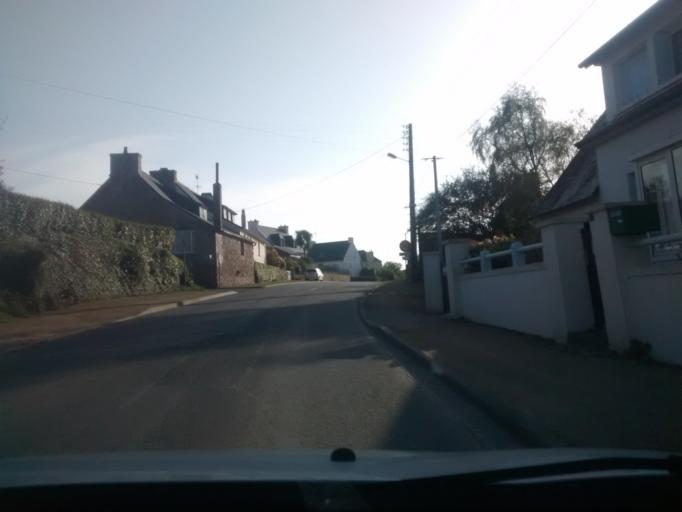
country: FR
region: Brittany
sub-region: Departement des Cotes-d'Armor
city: Trelevern
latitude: 48.8090
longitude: -3.3652
